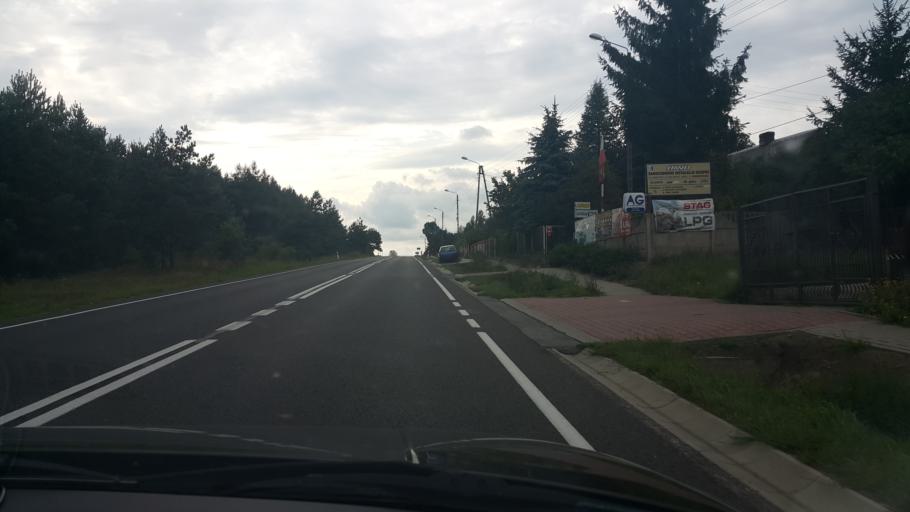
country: PL
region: Swietokrzyskie
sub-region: Powiat skarzyski
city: Blizyn
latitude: 51.0985
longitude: 20.7991
